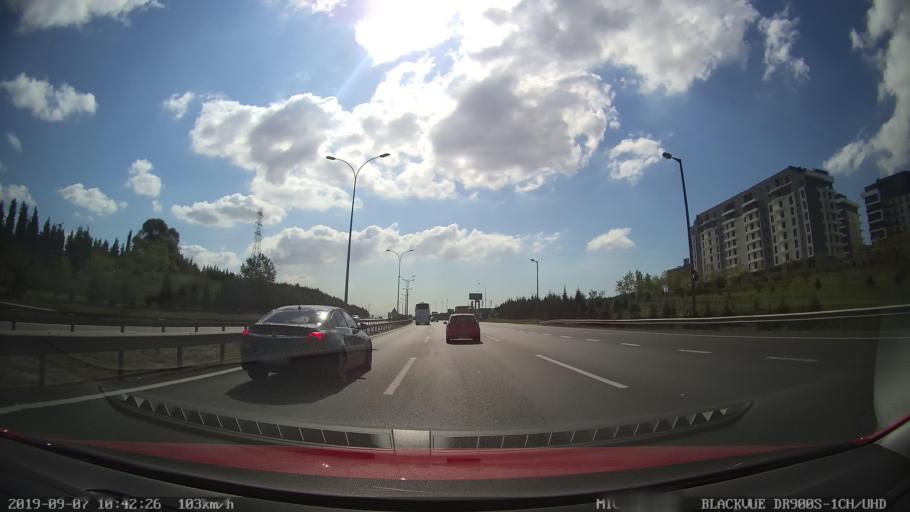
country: TR
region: Kocaeli
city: Balcik
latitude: 40.8403
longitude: 29.4173
